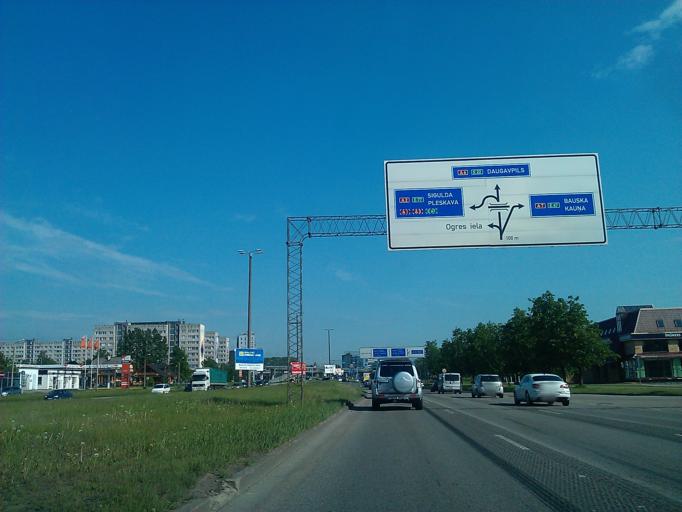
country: LV
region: Riga
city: Riga
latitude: 56.9266
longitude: 24.1586
